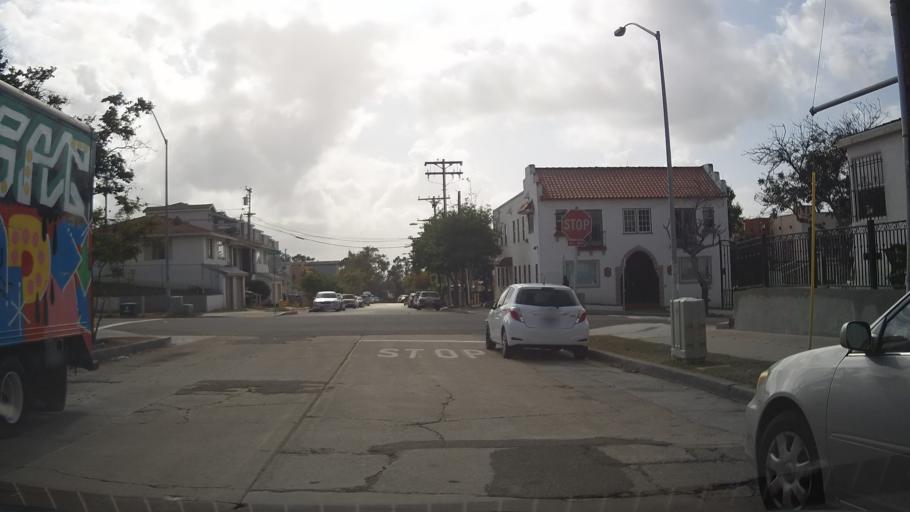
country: US
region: California
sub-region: San Diego County
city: San Diego
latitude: 32.7162
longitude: -117.1360
